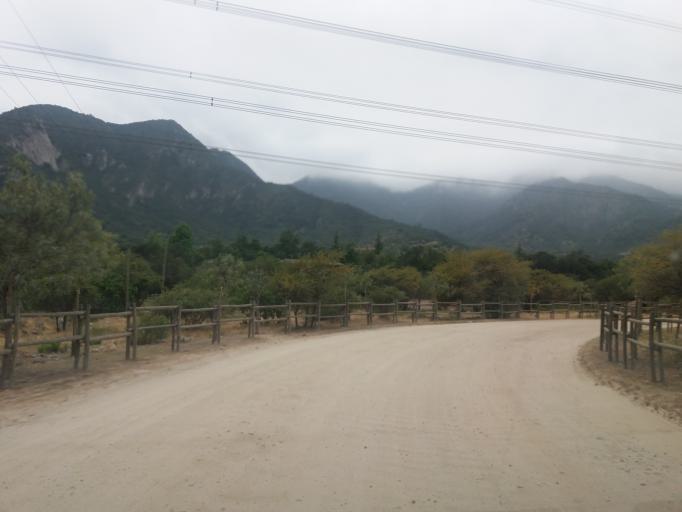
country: CL
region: Valparaiso
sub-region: Provincia de Marga Marga
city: Limache
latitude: -33.0276
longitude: -71.1411
